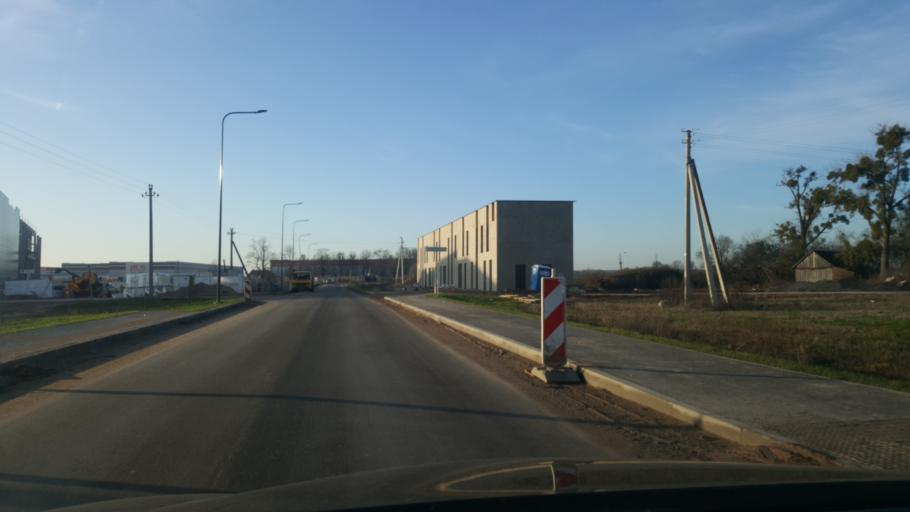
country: LT
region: Kauno apskritis
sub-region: Kauno rajonas
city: Mastaiciai
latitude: 54.8528
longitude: 23.8467
